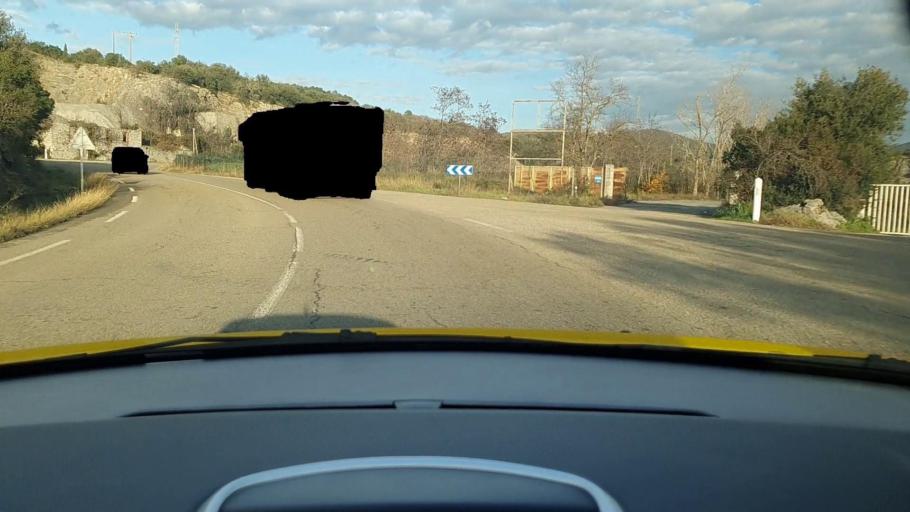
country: FR
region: Languedoc-Roussillon
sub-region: Departement du Gard
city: Saint-Martin-de-Valgalgues
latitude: 44.1722
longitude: 4.0835
